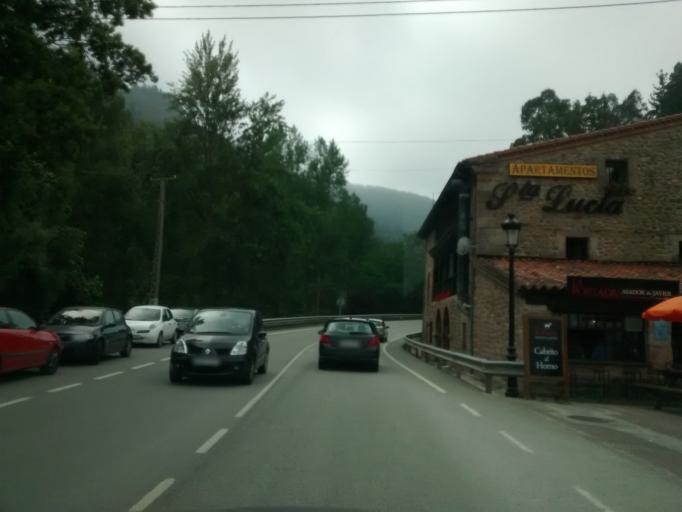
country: ES
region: Cantabria
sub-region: Provincia de Cantabria
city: Cabezon de la Sal
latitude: 43.2855
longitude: -4.2362
